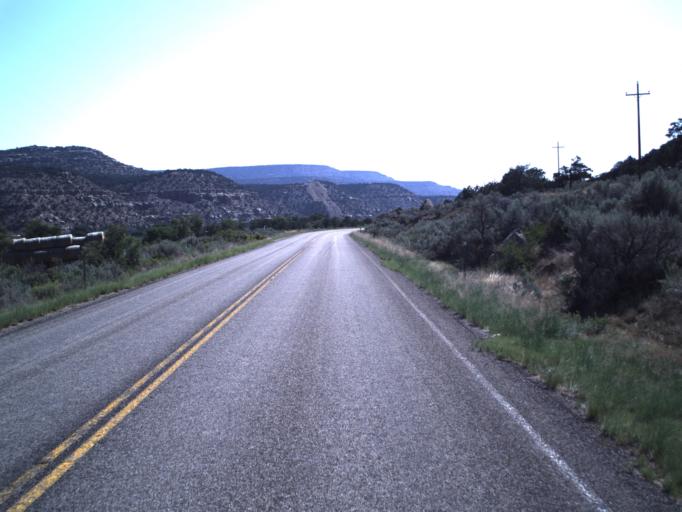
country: US
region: Utah
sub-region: Duchesne County
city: Duchesne
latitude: 40.2986
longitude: -110.5327
